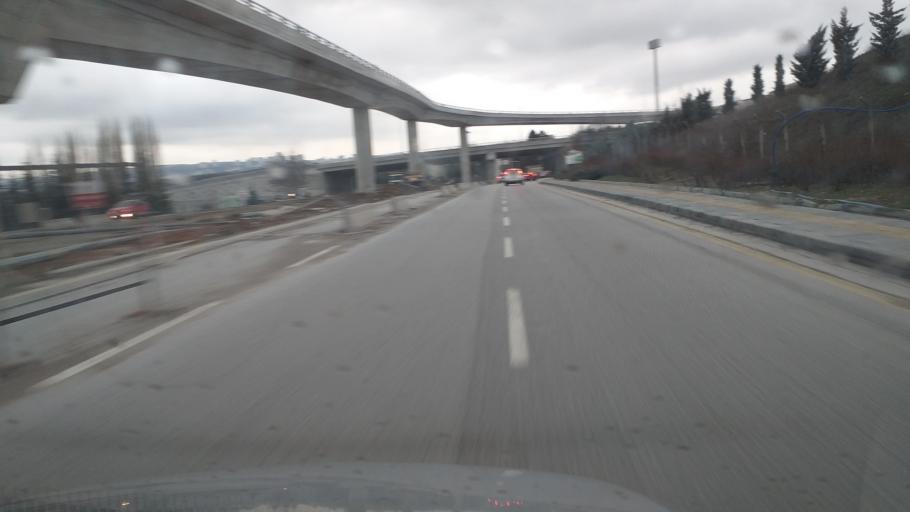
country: TR
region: Ankara
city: Batikent
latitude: 39.8983
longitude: 32.7334
